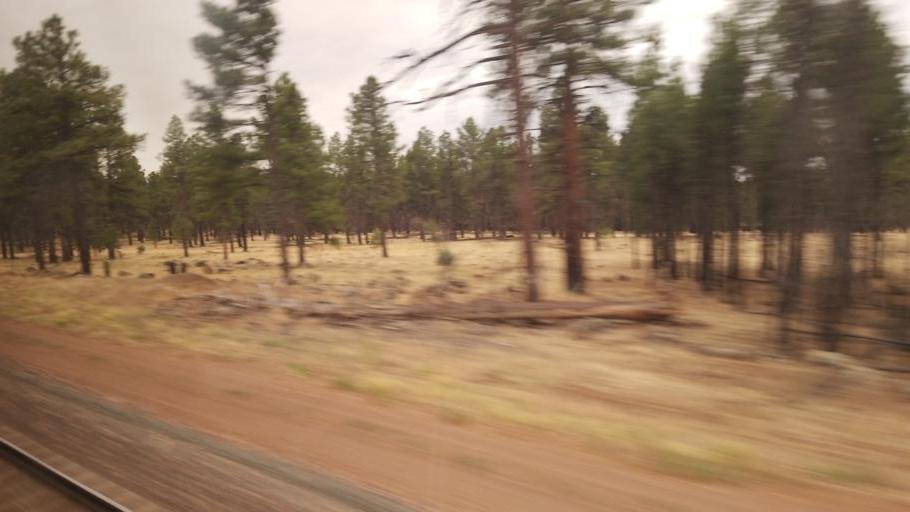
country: US
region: Arizona
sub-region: Coconino County
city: Parks
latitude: 35.2460
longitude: -112.0531
